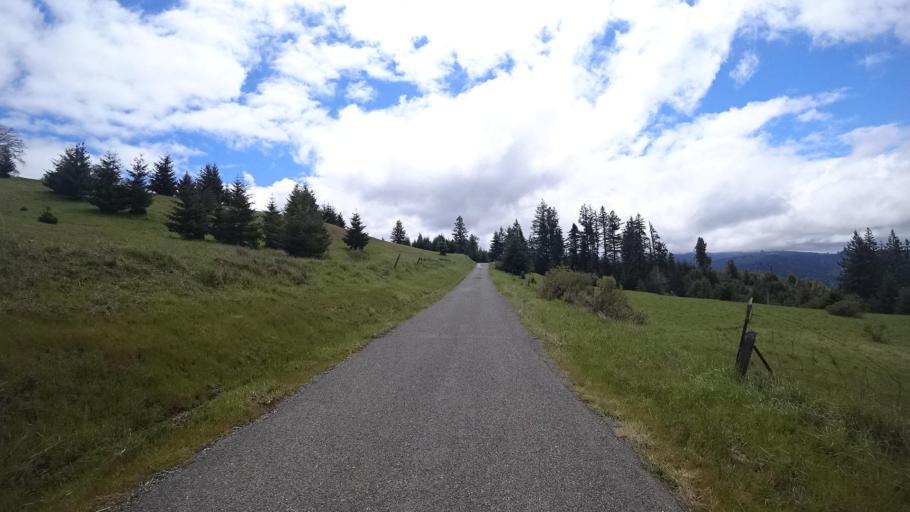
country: US
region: California
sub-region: Humboldt County
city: Blue Lake
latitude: 40.7898
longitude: -123.9676
